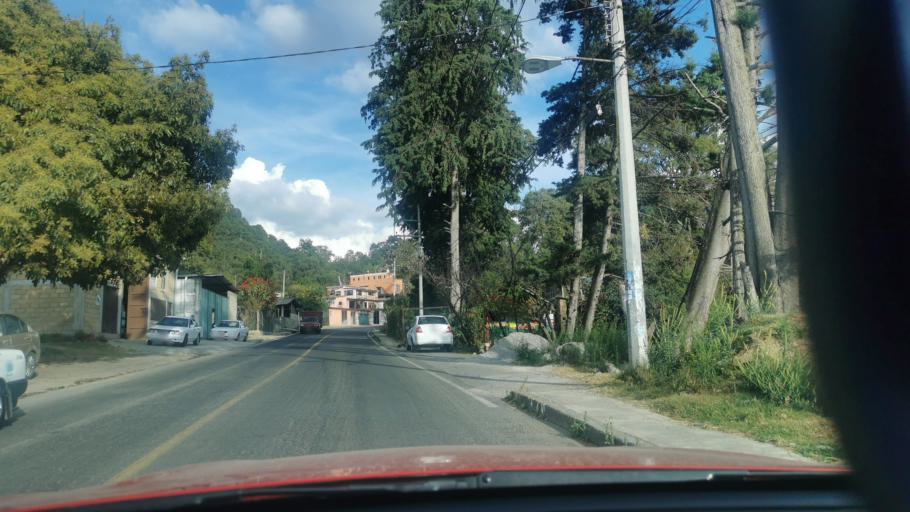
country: MX
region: Mexico
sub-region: Amanalco
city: Polvillos (San Bartolo Quinta Seccion)
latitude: 19.2358
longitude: -100.0766
